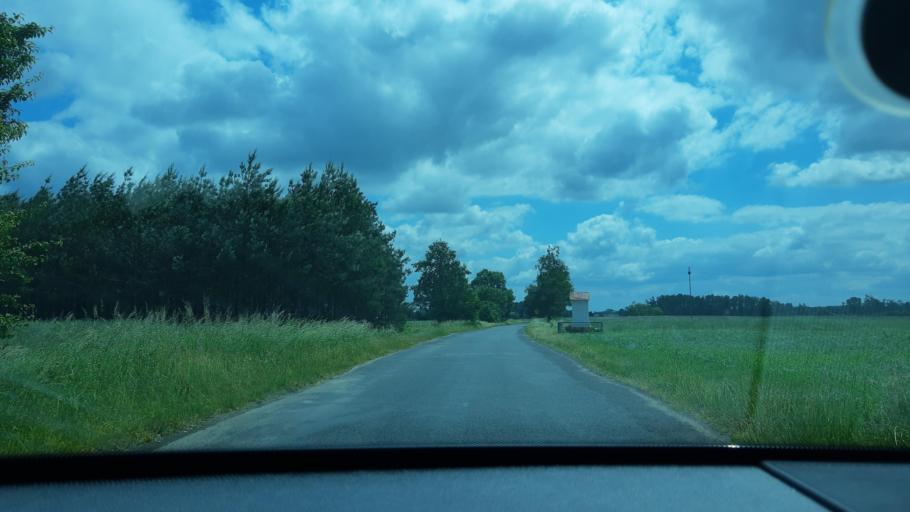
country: PL
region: Lodz Voivodeship
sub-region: Powiat zdunskowolski
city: Zapolice
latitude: 51.5391
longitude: 18.8236
